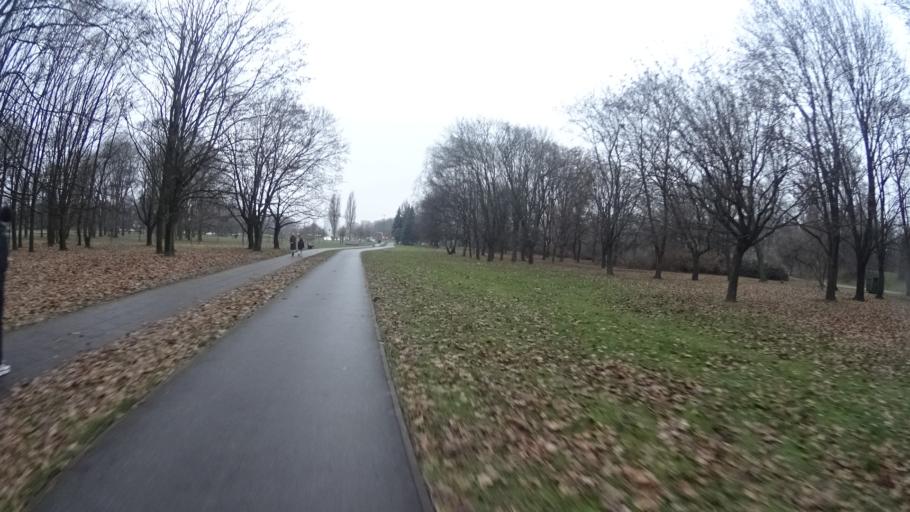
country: PL
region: Masovian Voivodeship
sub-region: Warszawa
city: Ochota
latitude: 52.2100
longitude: 20.9918
